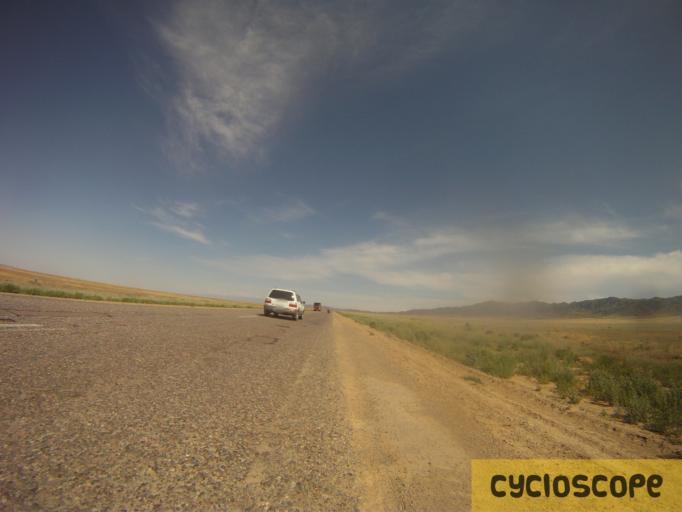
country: KZ
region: Almaty Oblysy
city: Kegen
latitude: 43.3868
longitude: 78.8387
